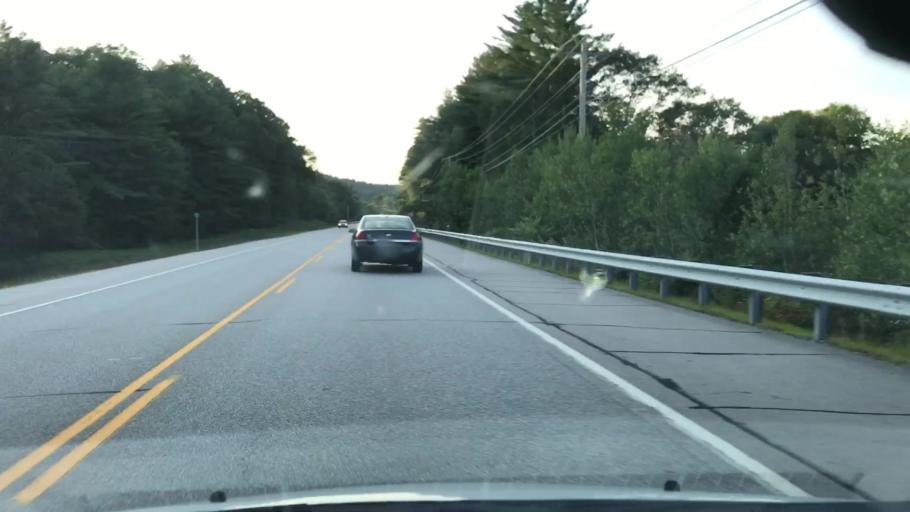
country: US
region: New Hampshire
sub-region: Grafton County
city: Rumney
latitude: 43.8078
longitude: -71.8619
